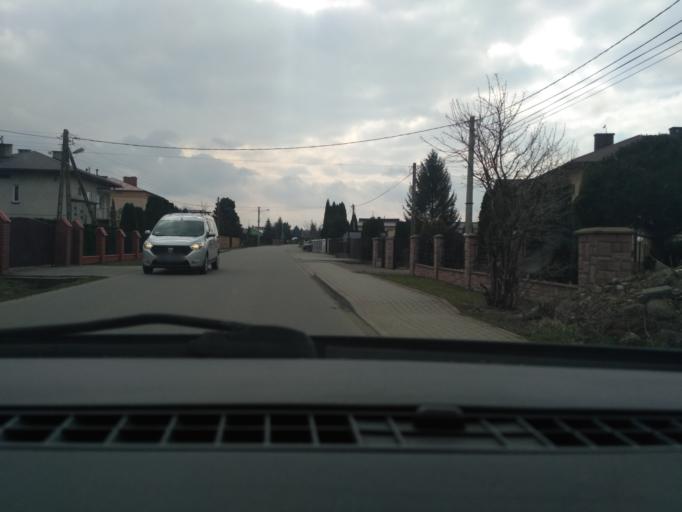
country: PL
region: Subcarpathian Voivodeship
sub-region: Powiat krosnienski
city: Kroscienko Wyzne
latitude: 49.6625
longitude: 21.8318
